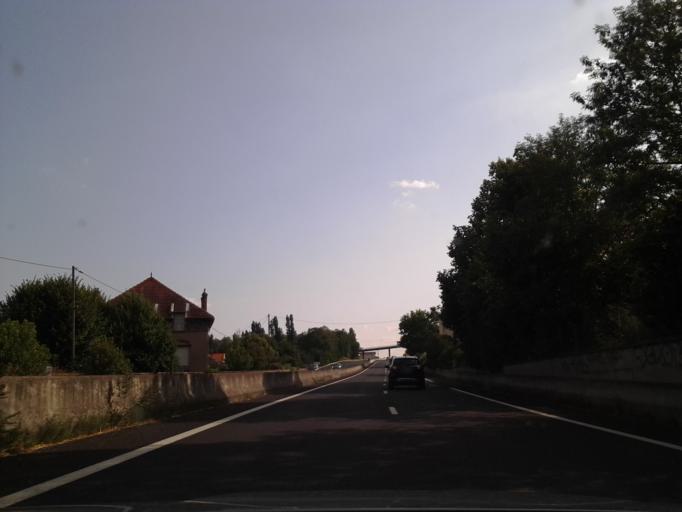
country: FR
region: Auvergne
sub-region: Departement du Puy-de-Dome
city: Le Breuil-sur-Couze
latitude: 45.5020
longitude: 3.2604
